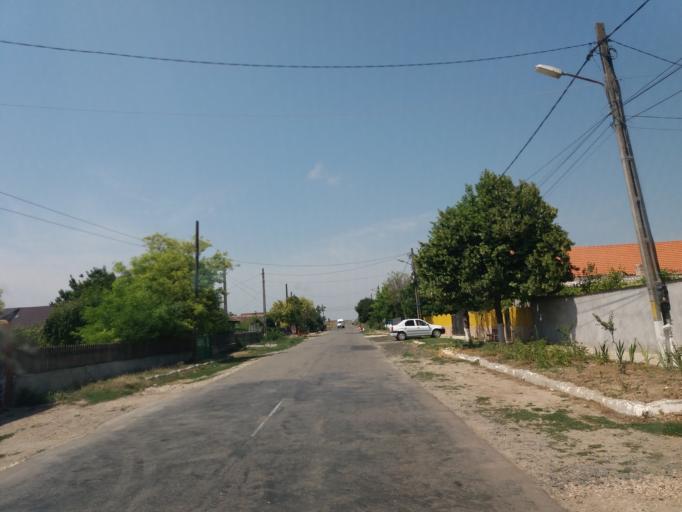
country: RO
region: Constanta
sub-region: Comuna Corbu
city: Corbu
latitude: 44.4222
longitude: 28.6603
